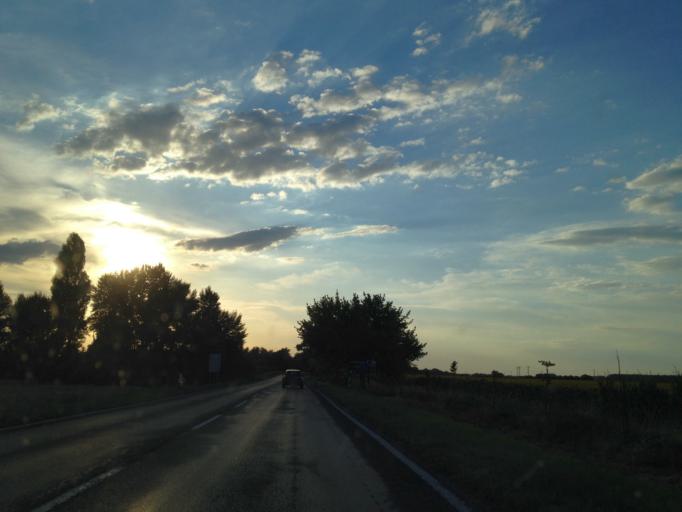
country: HU
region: Gyor-Moson-Sopron
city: Mosonszentmiklos
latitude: 47.7679
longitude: 17.4311
